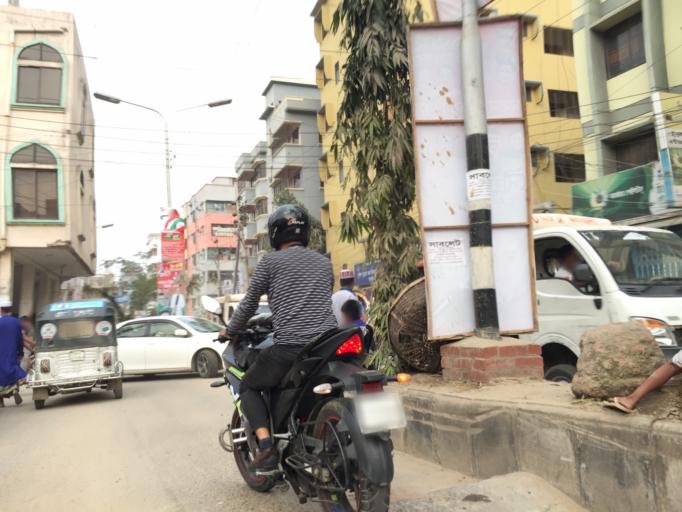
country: BD
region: Dhaka
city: Azimpur
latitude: 23.7824
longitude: 90.3685
